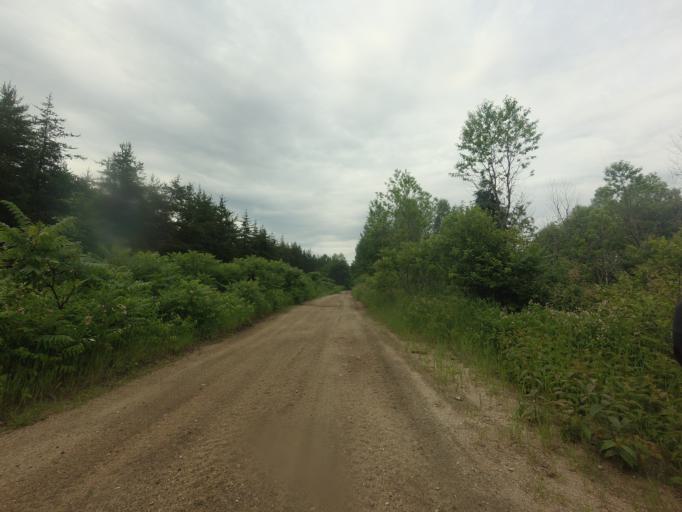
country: CA
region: Quebec
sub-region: Outaouais
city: Maniwaki
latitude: 46.3049
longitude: -76.0174
